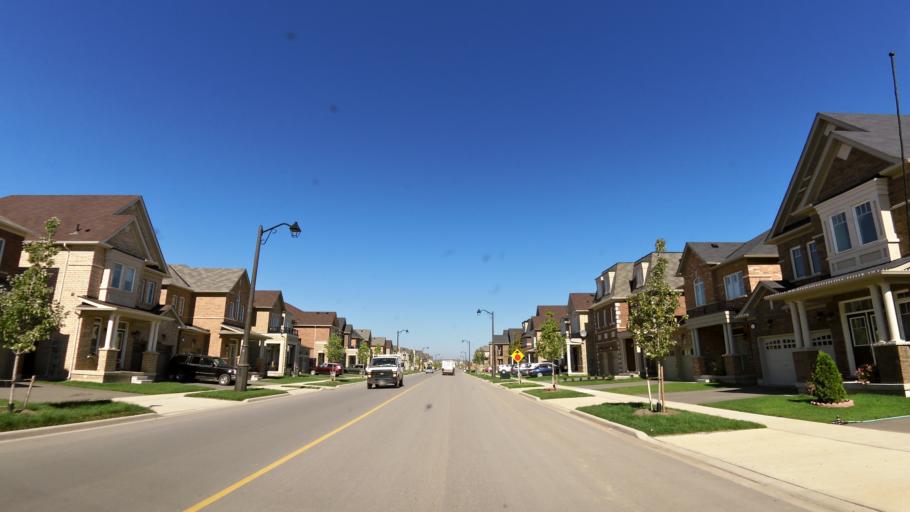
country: CA
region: Ontario
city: Oakville
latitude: 43.4754
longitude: -79.7390
